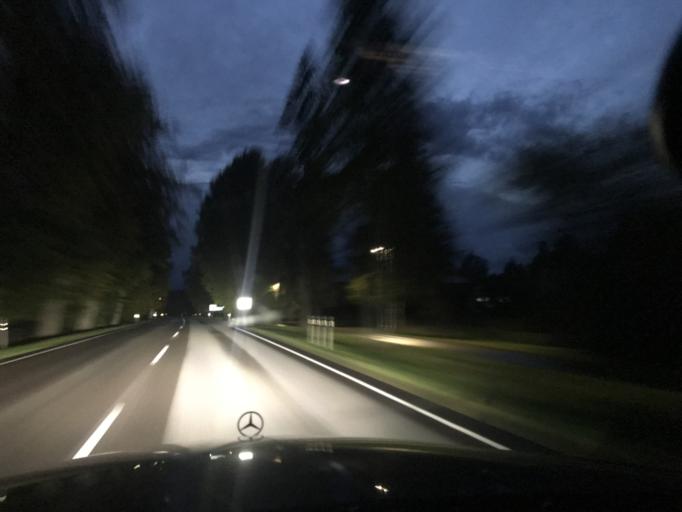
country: EE
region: Valgamaa
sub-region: Torva linn
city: Torva
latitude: 58.0129
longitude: 25.8866
